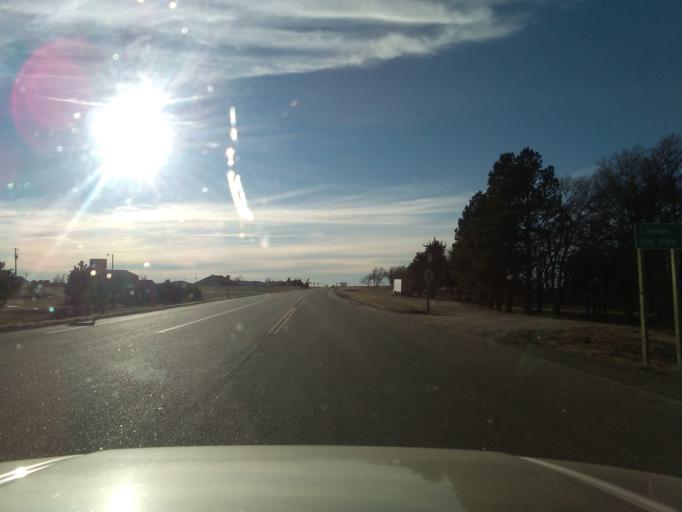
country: US
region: Kansas
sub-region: Sheridan County
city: Hoxie
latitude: 39.5423
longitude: -100.5719
